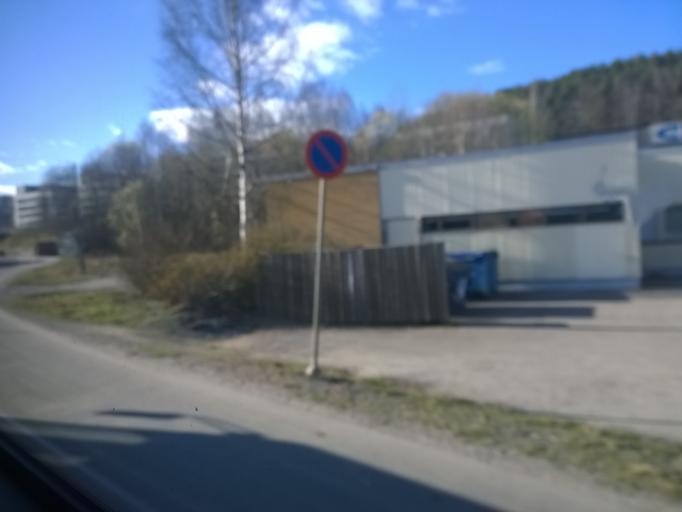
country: FI
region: Pirkanmaa
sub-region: Tampere
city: Tampere
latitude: 61.4908
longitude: 23.7930
